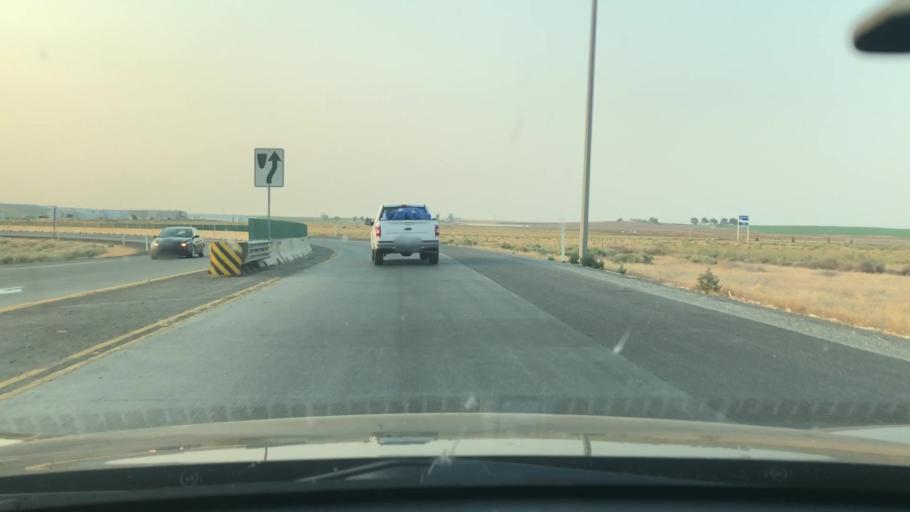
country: US
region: Washington
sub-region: Franklin County
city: Pasco
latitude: 46.2656
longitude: -119.0836
